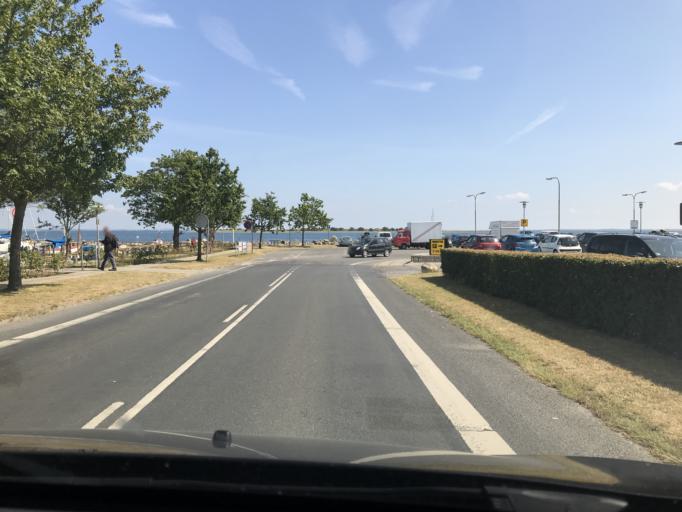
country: DK
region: South Denmark
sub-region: AEro Kommune
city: AEroskobing
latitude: 54.8919
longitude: 10.4104
